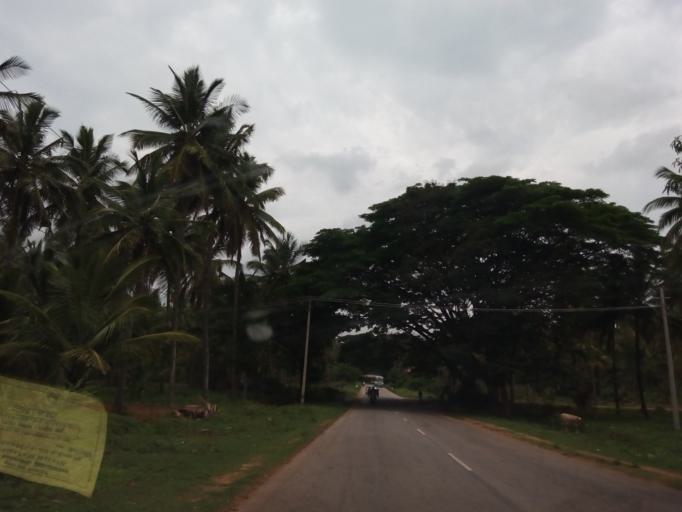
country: IN
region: Karnataka
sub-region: Hassan
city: Shravanabelagola
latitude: 12.8741
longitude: 76.4426
